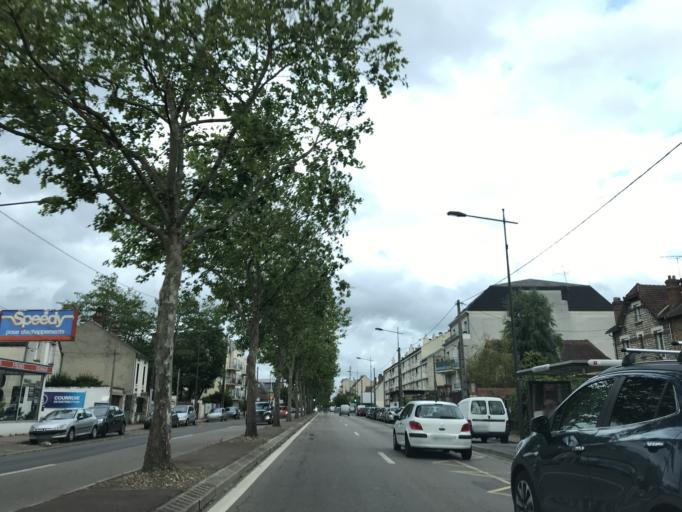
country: FR
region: Ile-de-France
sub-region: Departement des Yvelines
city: Mantes-la-Ville
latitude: 48.9943
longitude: 1.6960
